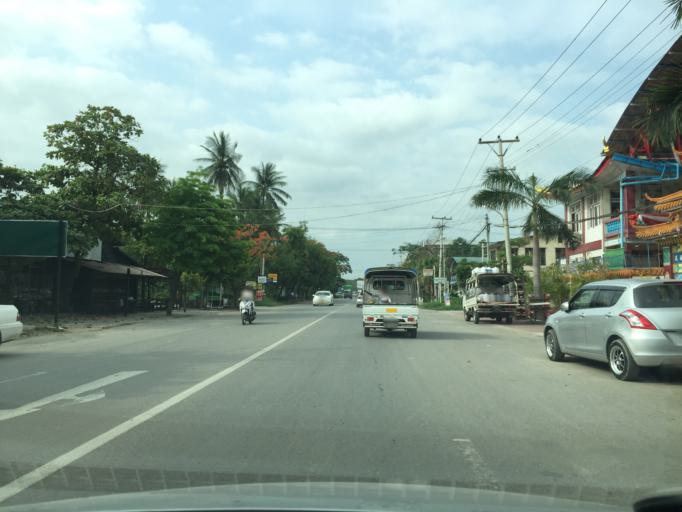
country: MM
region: Mandalay
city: Mandalay
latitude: 21.9725
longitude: 96.1031
